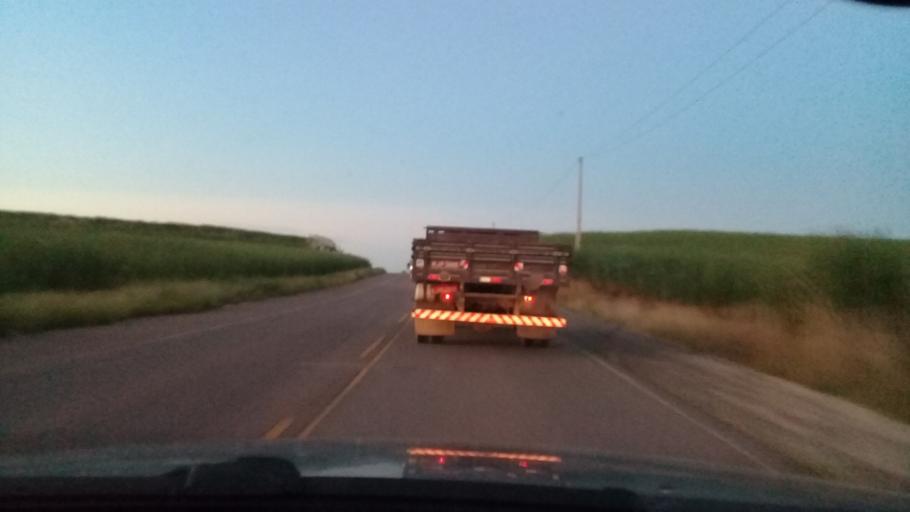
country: BR
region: Pernambuco
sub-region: Sirinhaem
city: Sirinhaem
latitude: -8.5527
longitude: -35.0930
